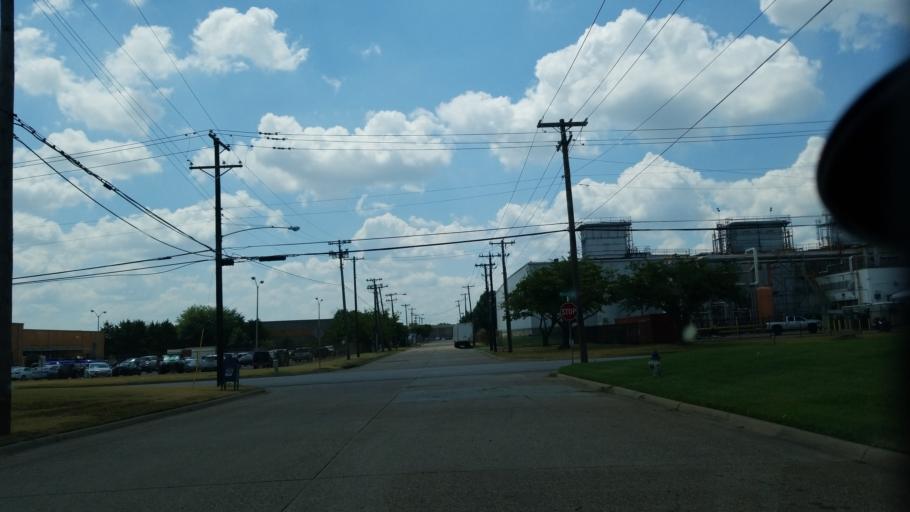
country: US
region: Texas
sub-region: Dallas County
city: Duncanville
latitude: 32.6856
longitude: -96.8864
